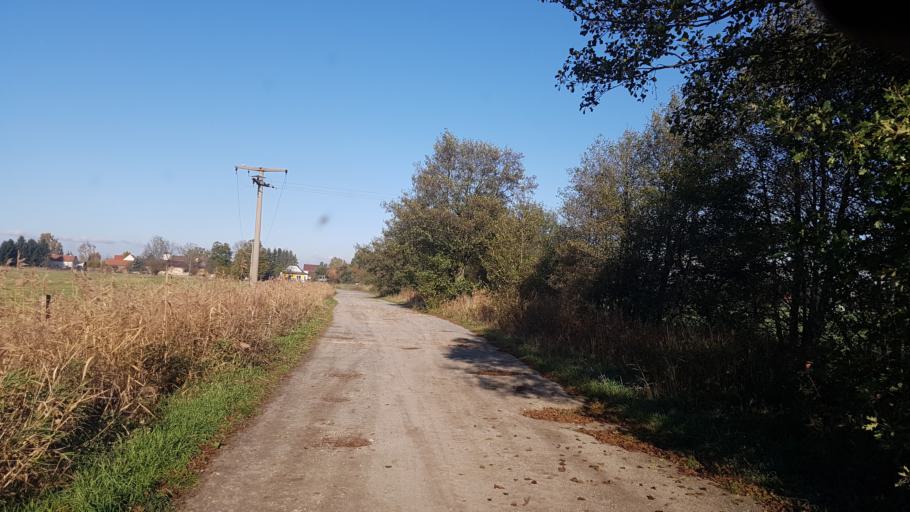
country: DE
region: Brandenburg
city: Ruckersdorf
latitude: 51.5604
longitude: 13.5438
